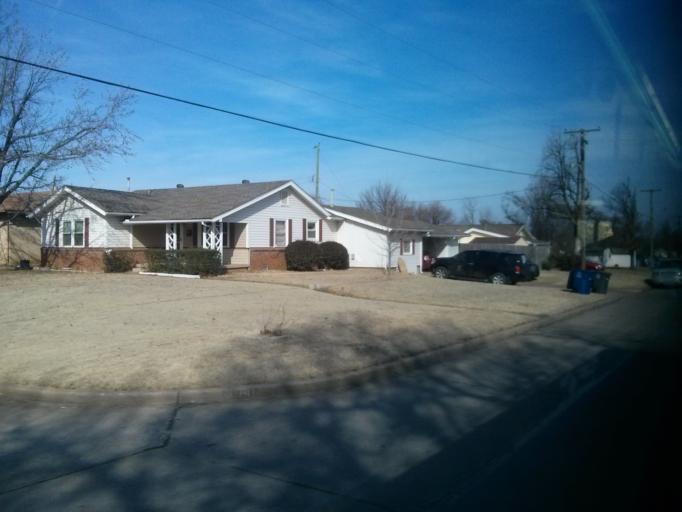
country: US
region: Oklahoma
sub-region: Tulsa County
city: Tulsa
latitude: 36.1558
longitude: -95.9314
